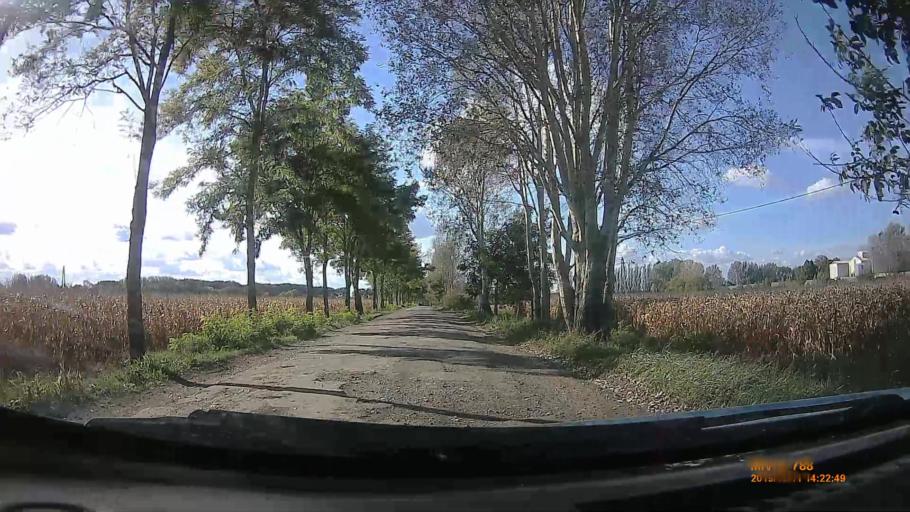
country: HU
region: Hajdu-Bihar
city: Hajduszoboszlo
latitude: 47.5289
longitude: 21.3630
